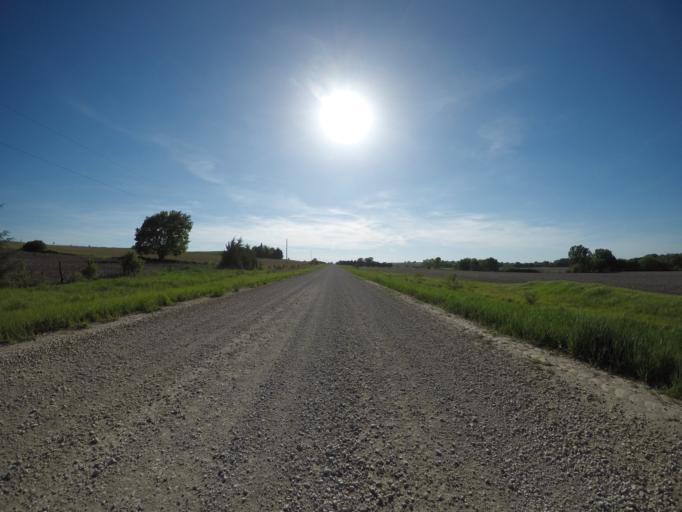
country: US
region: Kansas
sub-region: Clay County
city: Clay Center
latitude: 39.5102
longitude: -97.0196
